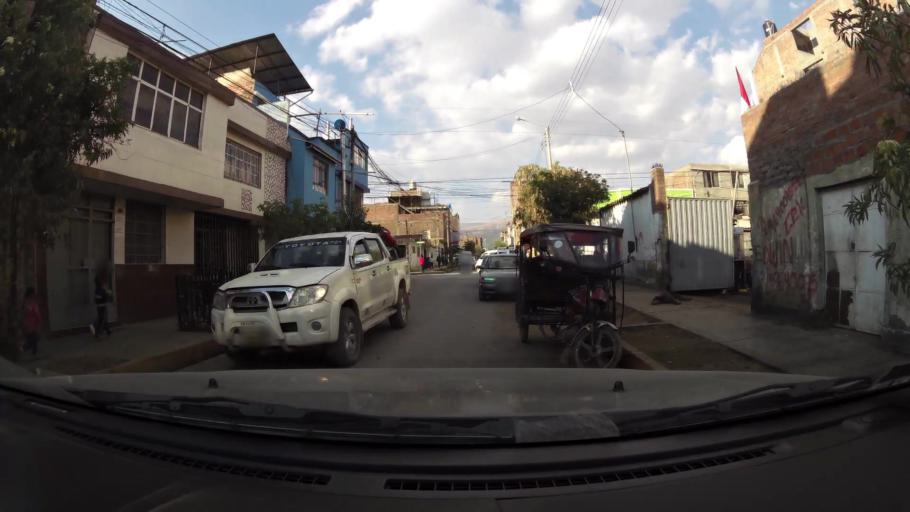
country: PE
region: Junin
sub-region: Provincia de Huancayo
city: El Tambo
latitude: -12.0528
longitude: -75.2184
